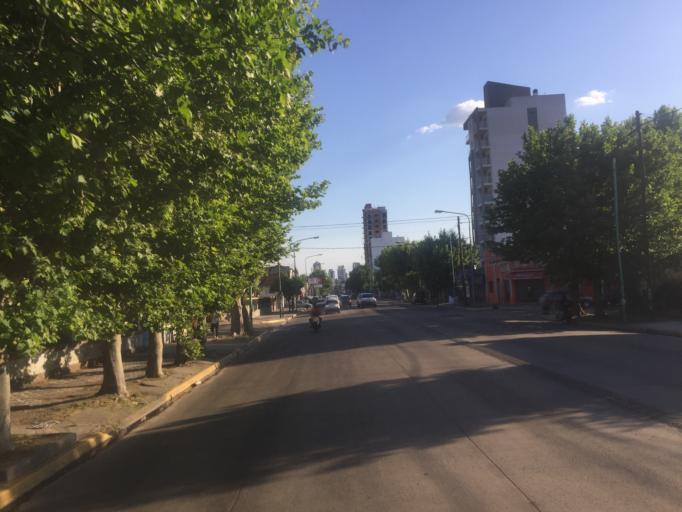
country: AR
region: Buenos Aires
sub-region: Partido de Lomas de Zamora
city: Lomas de Zamora
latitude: -34.7490
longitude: -58.3942
